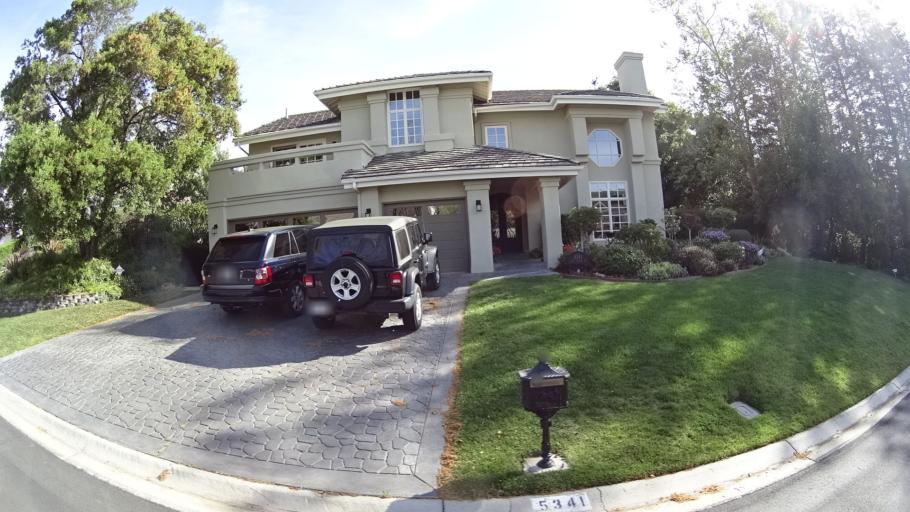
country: US
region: California
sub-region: Ventura County
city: Oak Park
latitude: 34.1906
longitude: -118.7965
